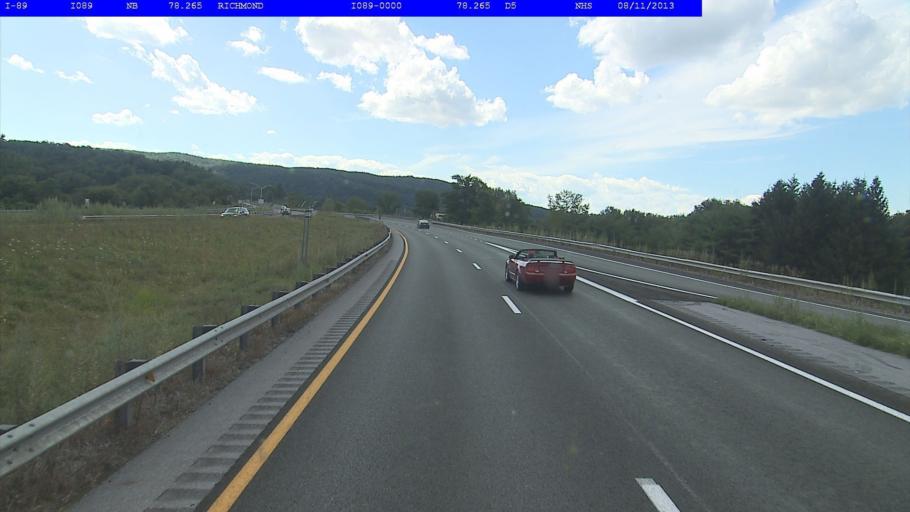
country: US
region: Vermont
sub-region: Chittenden County
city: Williston
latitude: 44.4240
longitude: -73.0084
